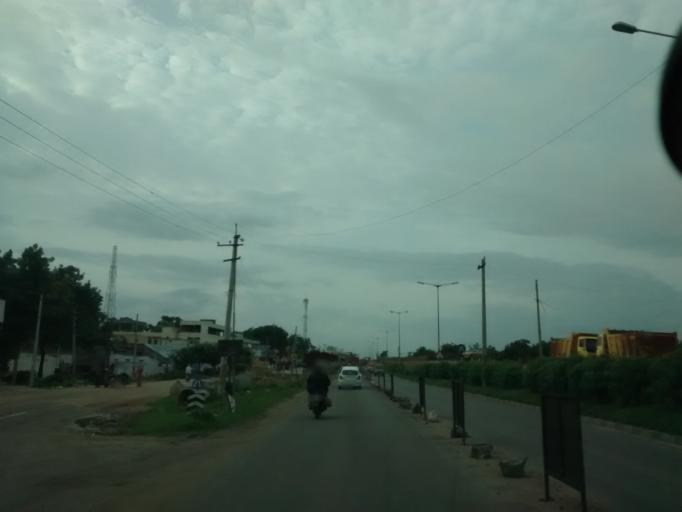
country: IN
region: Telangana
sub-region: Mahbubnagar
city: Gopalur
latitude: 16.5081
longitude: 77.9340
